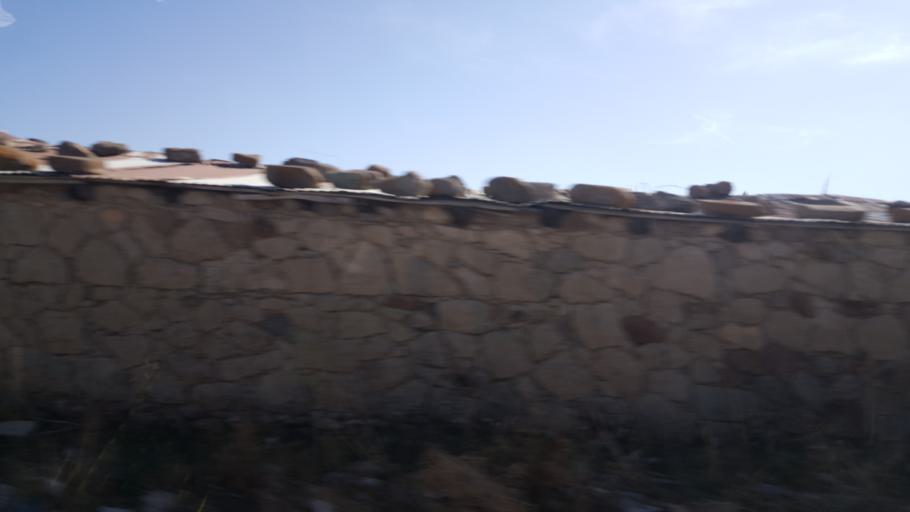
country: TR
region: Ankara
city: Yenice
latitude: 39.2741
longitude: 32.6736
